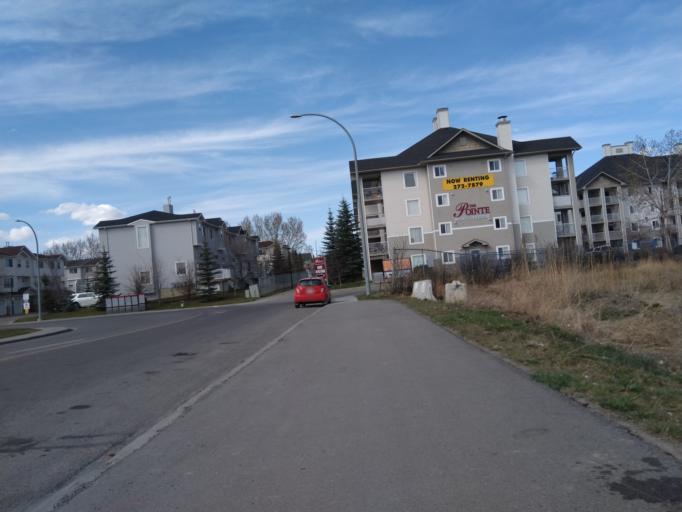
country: CA
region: Alberta
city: Chestermere
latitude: 51.0384
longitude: -113.9301
